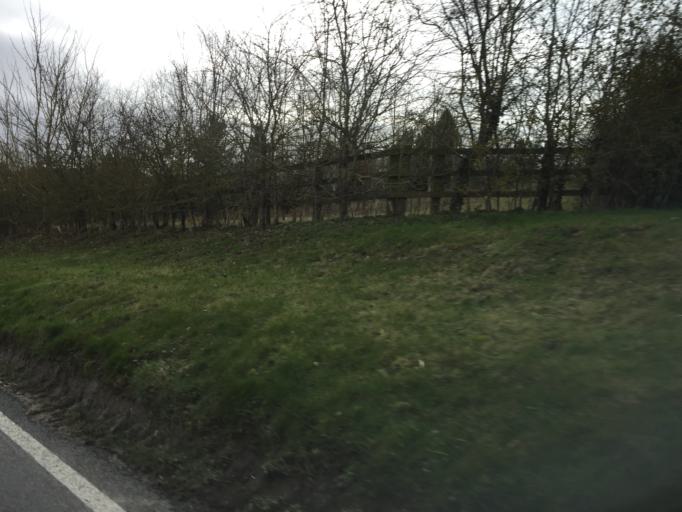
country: GB
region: England
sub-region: Oxfordshire
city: Goring
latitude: 51.5409
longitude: -1.1586
